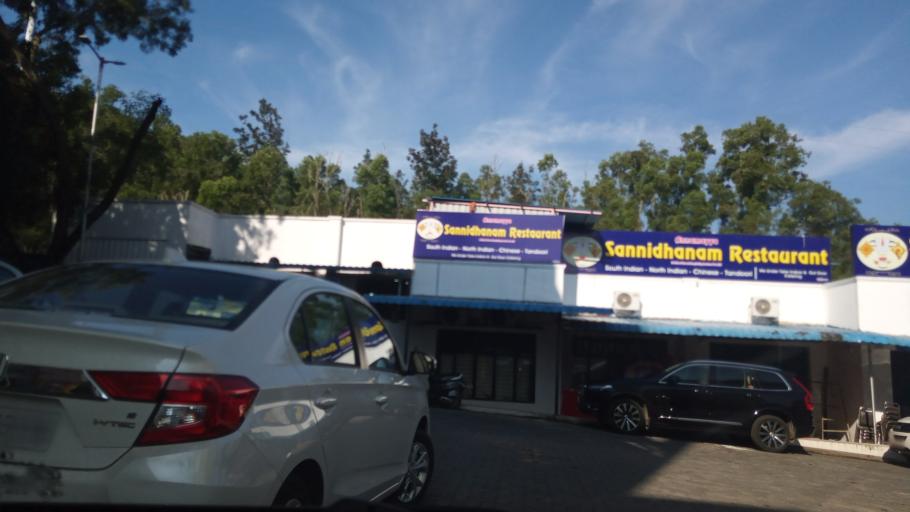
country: IN
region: Andhra Pradesh
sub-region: Chittoor
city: Tirumala
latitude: 13.6715
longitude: 79.3485
